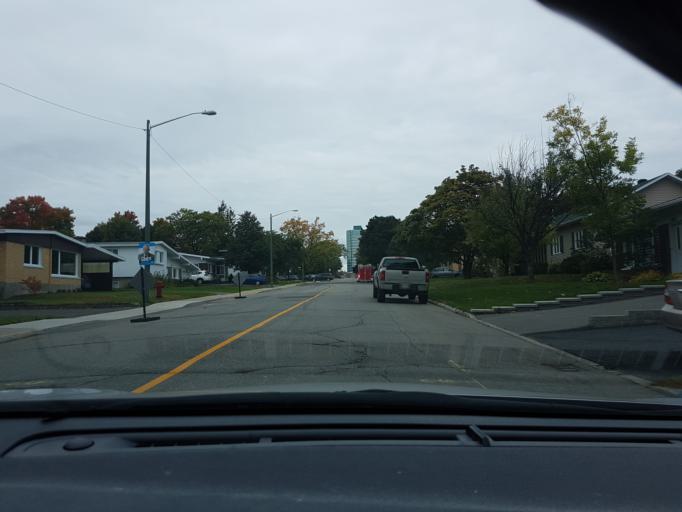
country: CA
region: Quebec
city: Quebec
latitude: 46.7666
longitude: -71.2765
